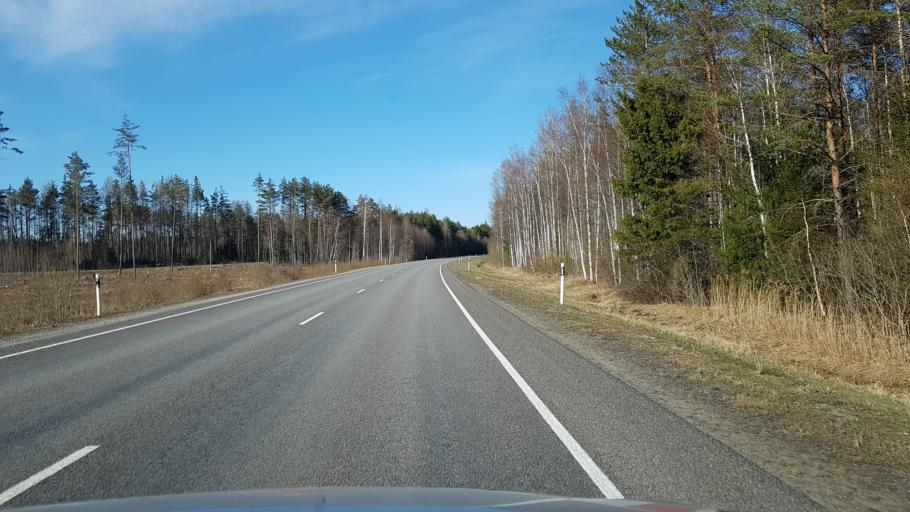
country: EE
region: Ida-Virumaa
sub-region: Kohtla-Nomme vald
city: Kohtla-Nomme
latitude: 59.0229
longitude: 27.2268
